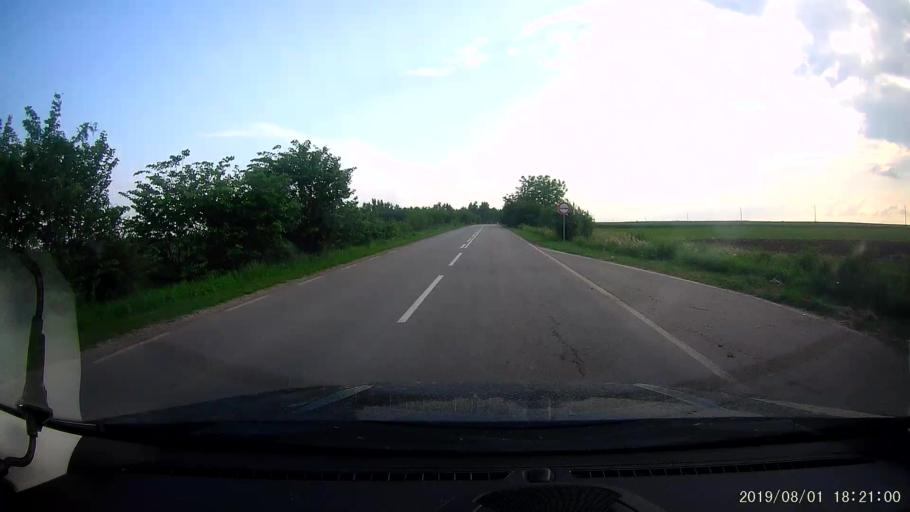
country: BG
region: Shumen
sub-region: Obshtina Kaolinovo
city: Kaolinovo
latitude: 43.6597
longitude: 27.0794
